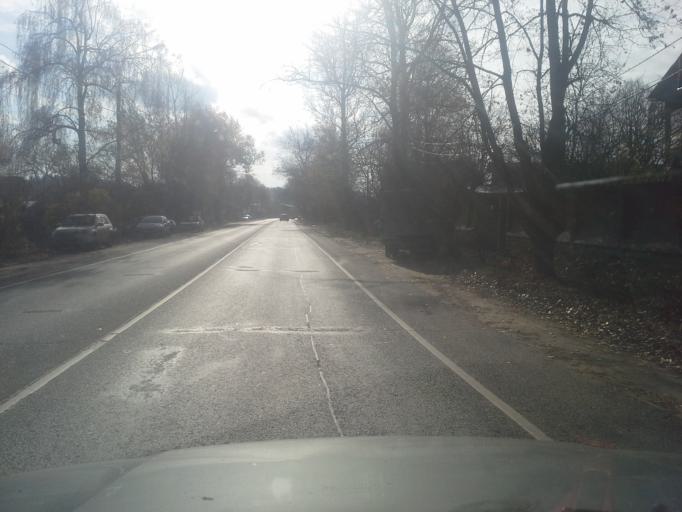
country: RU
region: Moskovskaya
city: Zvenigorod
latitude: 55.7193
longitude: 36.8651
